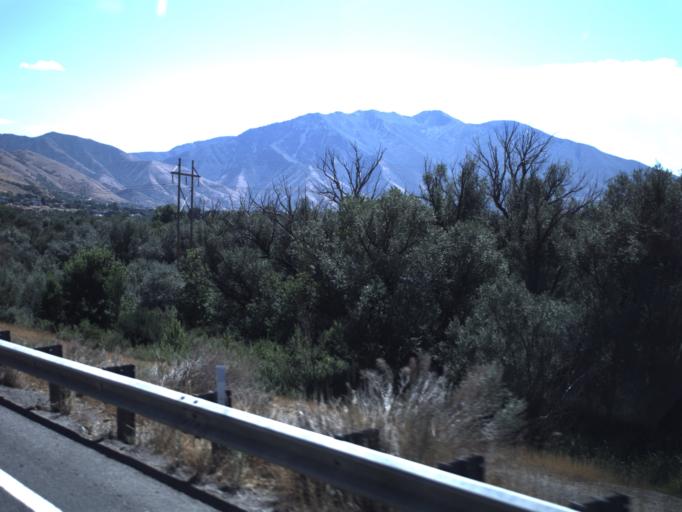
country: US
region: Utah
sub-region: Utah County
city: Springville
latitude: 40.1861
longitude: -111.6200
